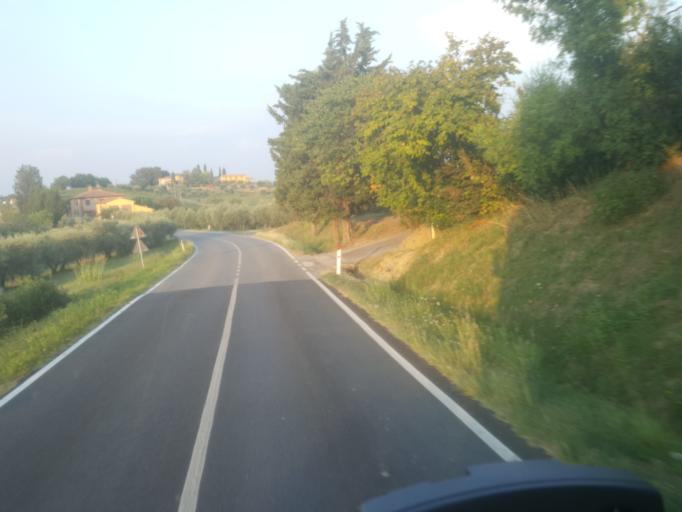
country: IT
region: Tuscany
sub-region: Province of Florence
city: Gambassi Terme
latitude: 43.5405
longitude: 10.9896
